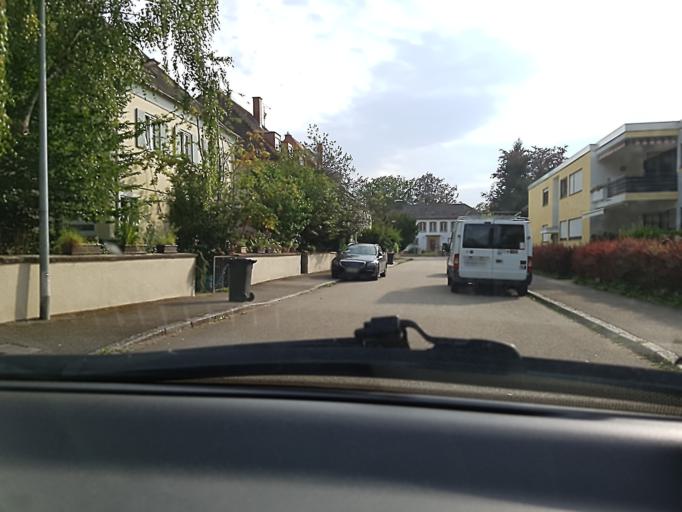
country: DE
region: Baden-Wuerttemberg
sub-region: Freiburg Region
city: Offenburg
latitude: 48.4633
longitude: 7.9567
